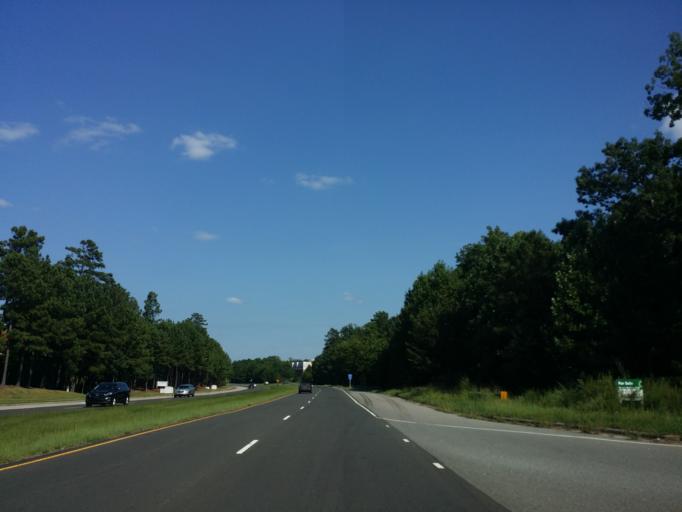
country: US
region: North Carolina
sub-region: Wake County
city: Morrisville
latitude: 35.9179
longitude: -78.7961
